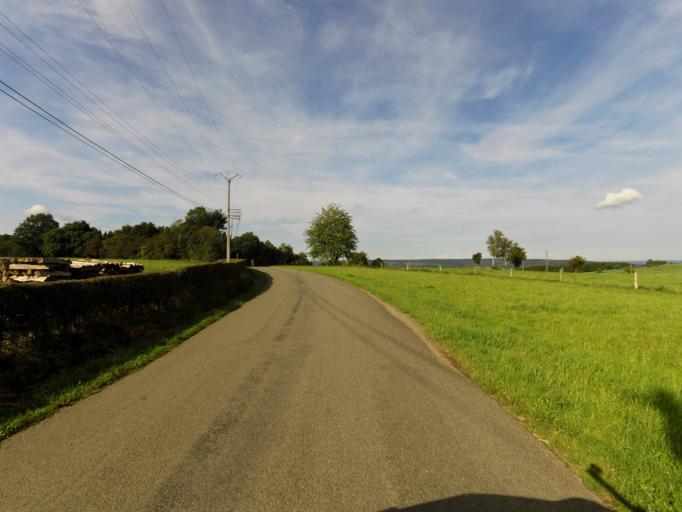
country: BE
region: Wallonia
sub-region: Province du Luxembourg
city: Rendeux
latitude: 50.2370
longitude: 5.5408
